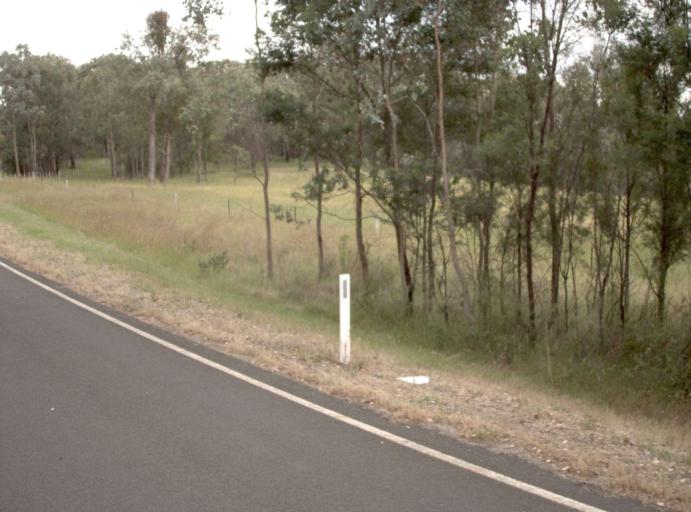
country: AU
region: Victoria
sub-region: East Gippsland
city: Bairnsdale
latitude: -37.7201
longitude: 147.3137
